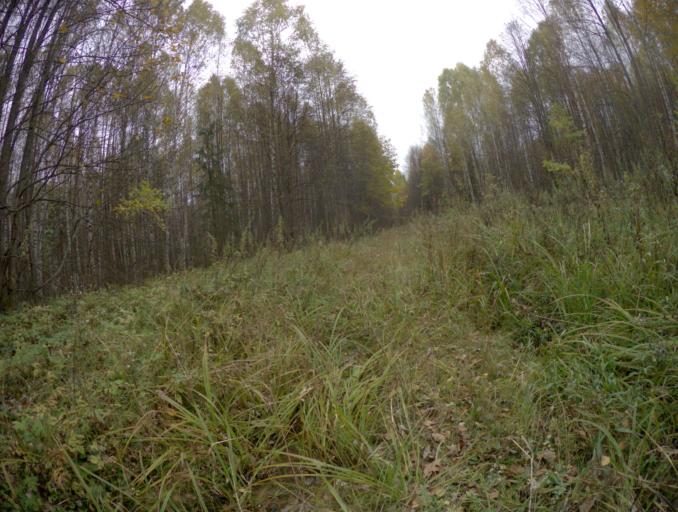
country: RU
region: Vladimir
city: Mstera
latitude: 56.3109
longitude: 41.7545
